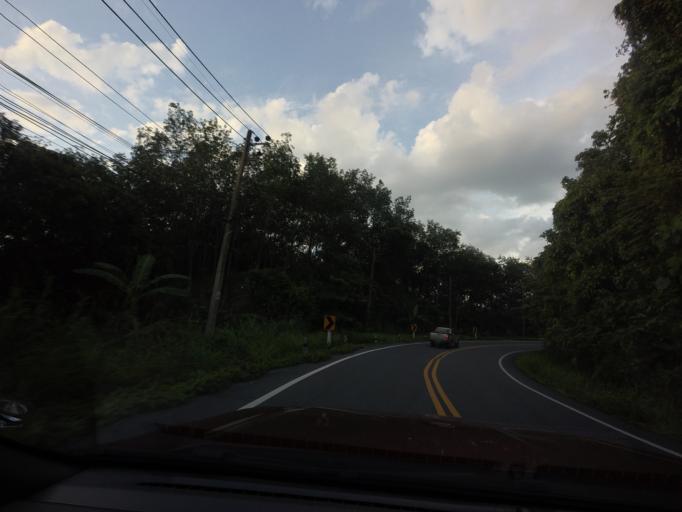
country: TH
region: Yala
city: Than To
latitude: 6.0390
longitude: 101.2062
